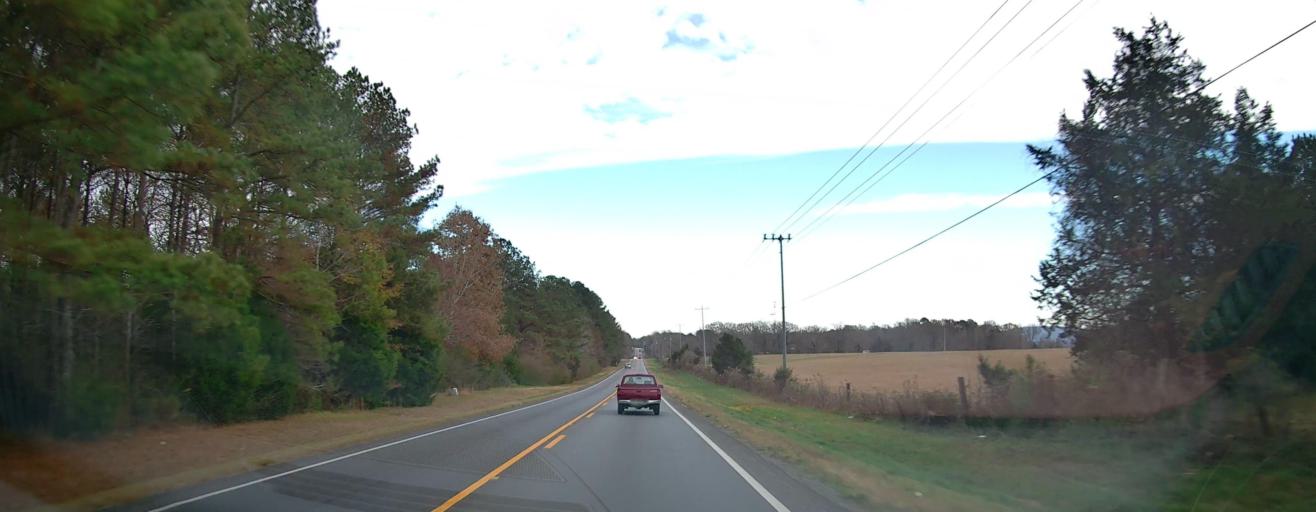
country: US
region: Alabama
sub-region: Morgan County
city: Priceville
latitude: 34.4782
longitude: -86.8172
